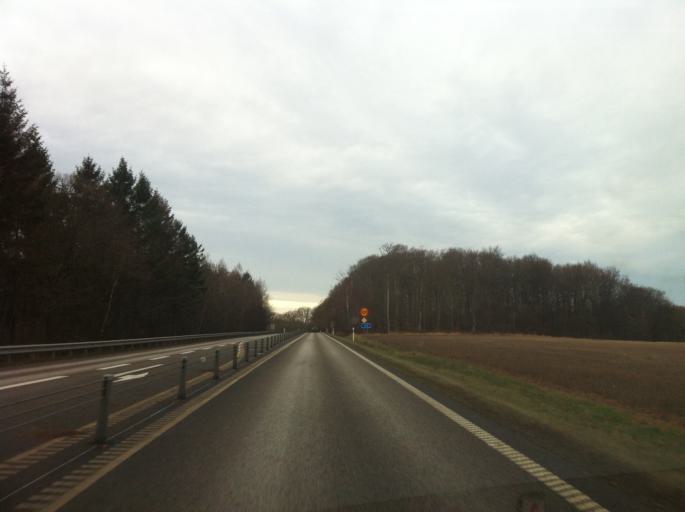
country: DK
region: Capital Region
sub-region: Helsingor Kommune
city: Hellebaek
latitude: 56.1228
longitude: 12.6195
